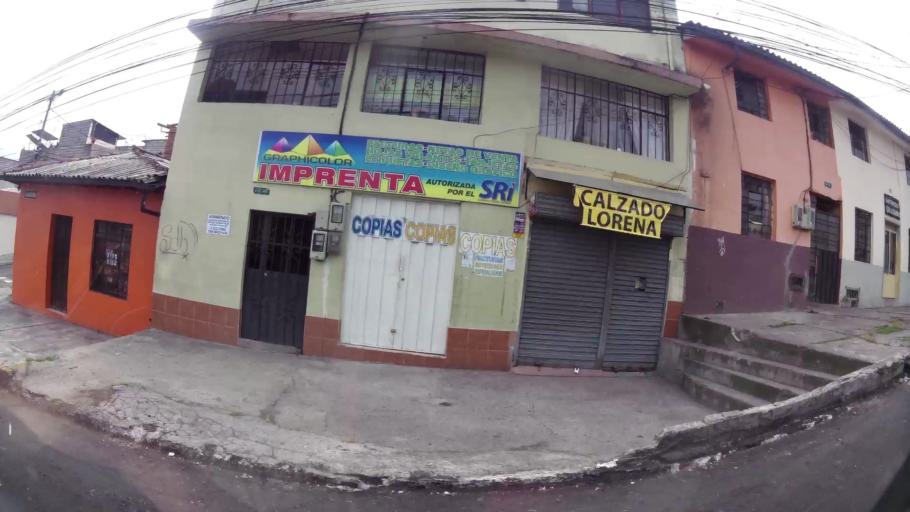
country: EC
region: Pichincha
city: Quito
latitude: -0.2121
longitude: -78.4839
